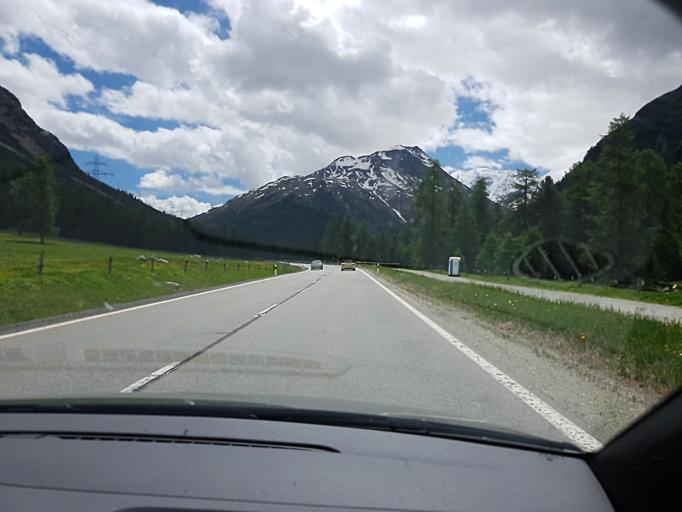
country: CH
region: Grisons
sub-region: Maloja District
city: Pontresina
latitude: 46.4690
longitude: 9.9286
